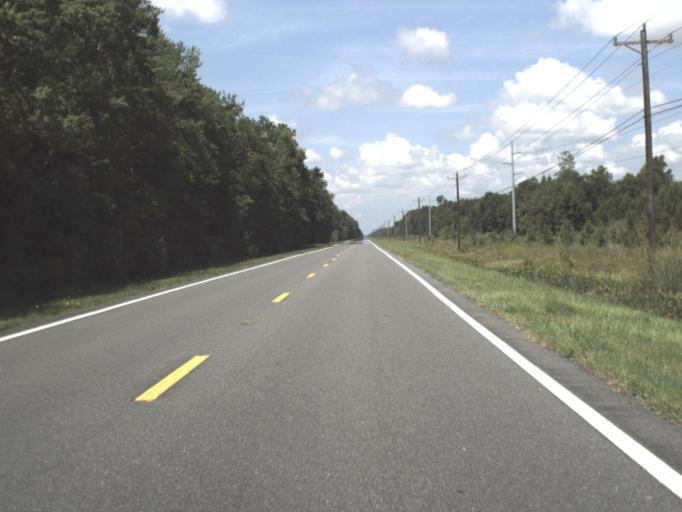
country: US
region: Florida
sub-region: Levy County
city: Chiefland
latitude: 29.2950
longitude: -82.8258
